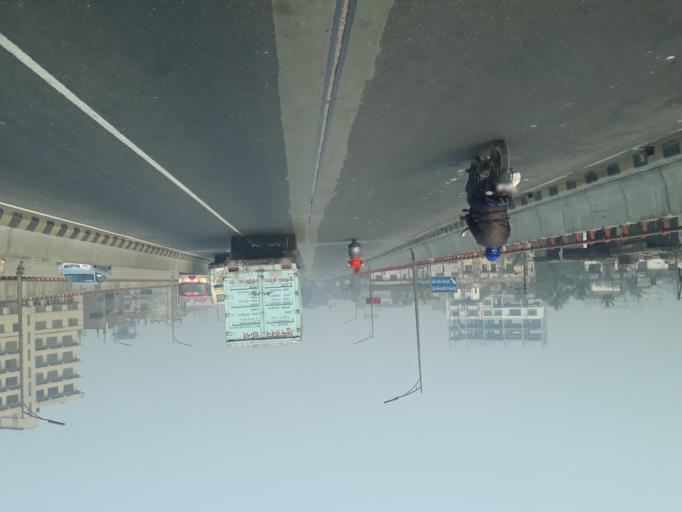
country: BD
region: Dhaka
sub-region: Dhaka
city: Dhaka
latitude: 23.7104
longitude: 90.4330
